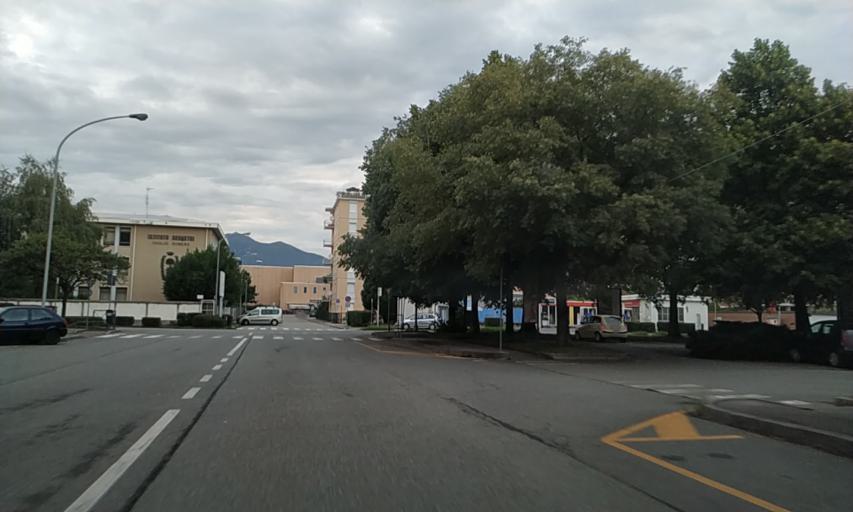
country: IT
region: Piedmont
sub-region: Provincia di Biella
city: Ponderano
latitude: 45.5523
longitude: 8.0540
